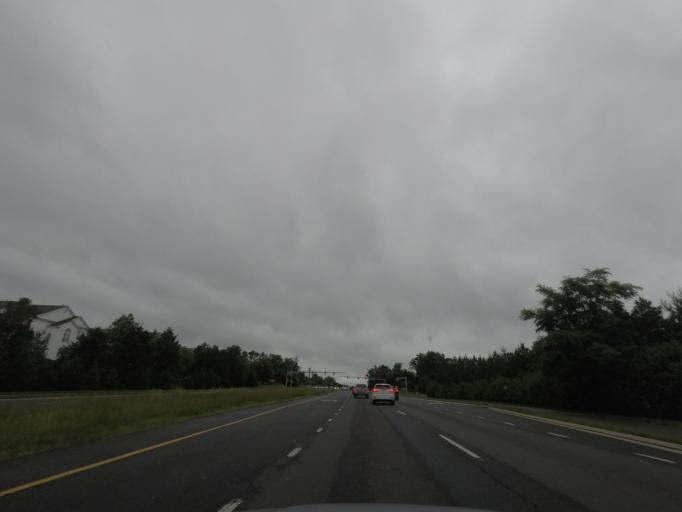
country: US
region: Virginia
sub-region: Prince William County
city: Haymarket
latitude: 38.8255
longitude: -77.6335
